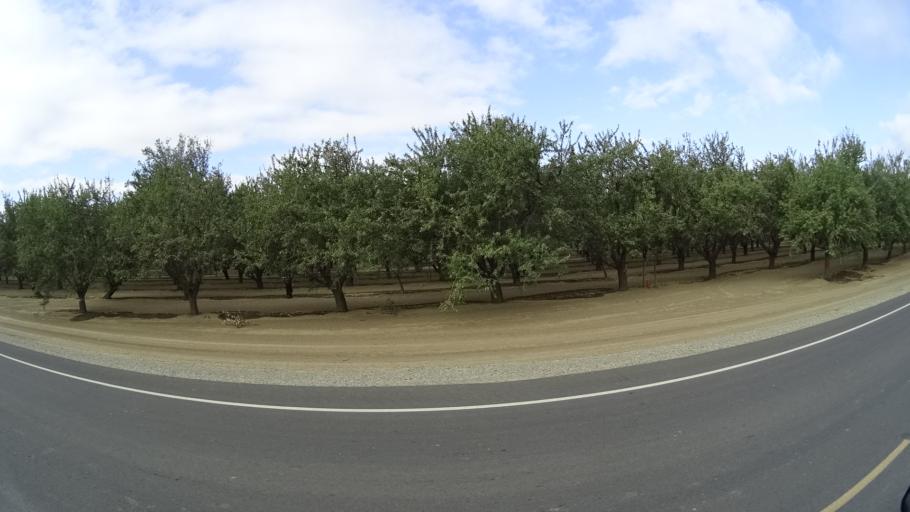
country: US
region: California
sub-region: Yolo County
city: Esparto
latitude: 38.7251
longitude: -122.0078
